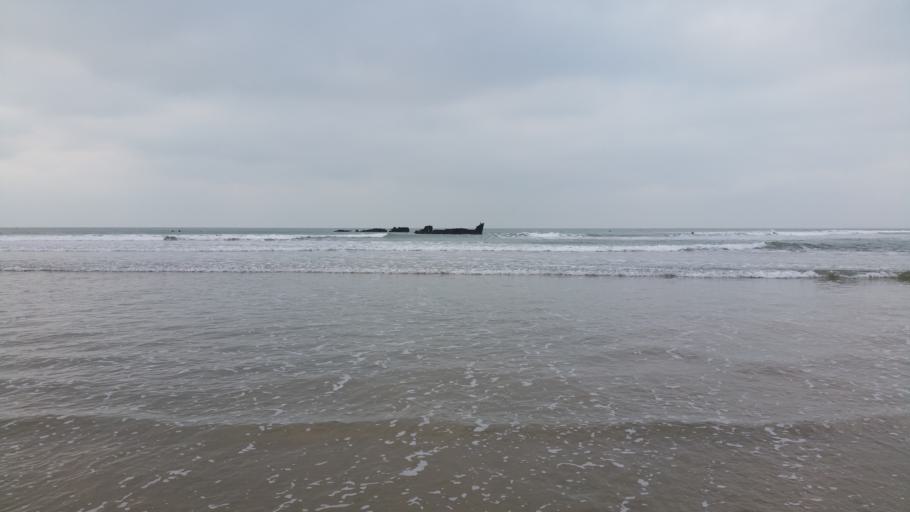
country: FR
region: Poitou-Charentes
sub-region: Departement de la Charente-Maritime
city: Saint-Trojan-les-Bains
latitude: 45.8419
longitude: -1.2522
